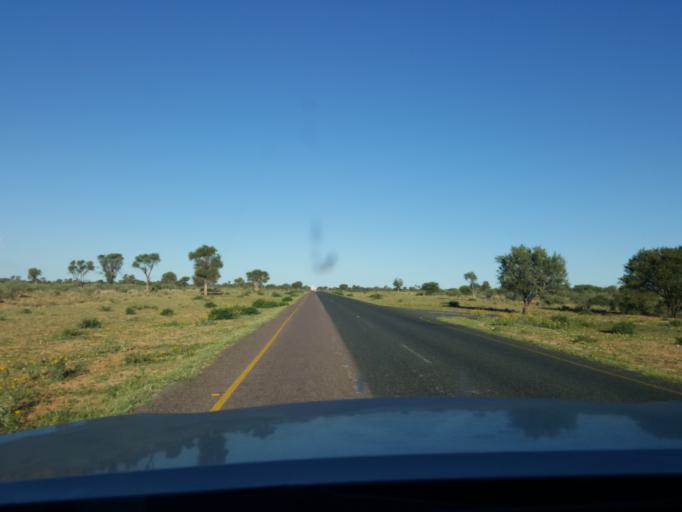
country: BW
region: Southern
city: Khakhea
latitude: -24.2582
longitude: 23.3086
